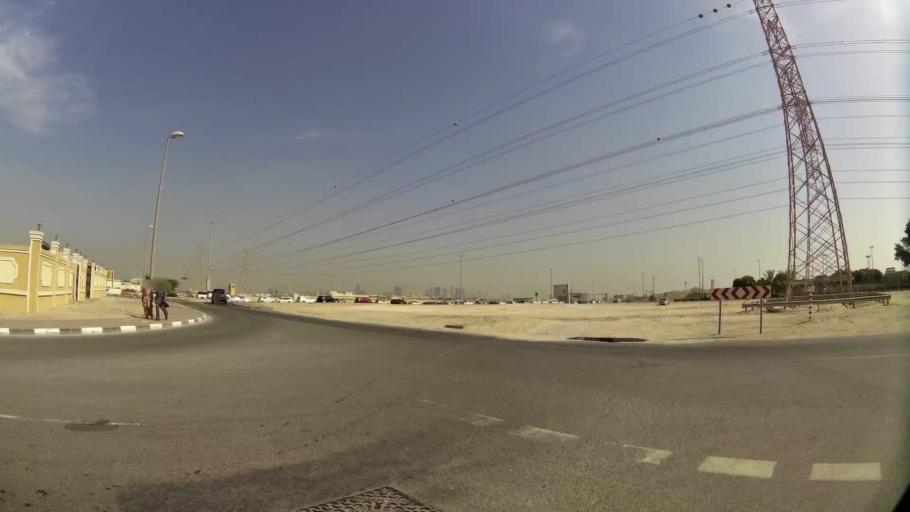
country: AE
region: Ash Shariqah
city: Sharjah
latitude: 25.2685
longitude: 55.3959
